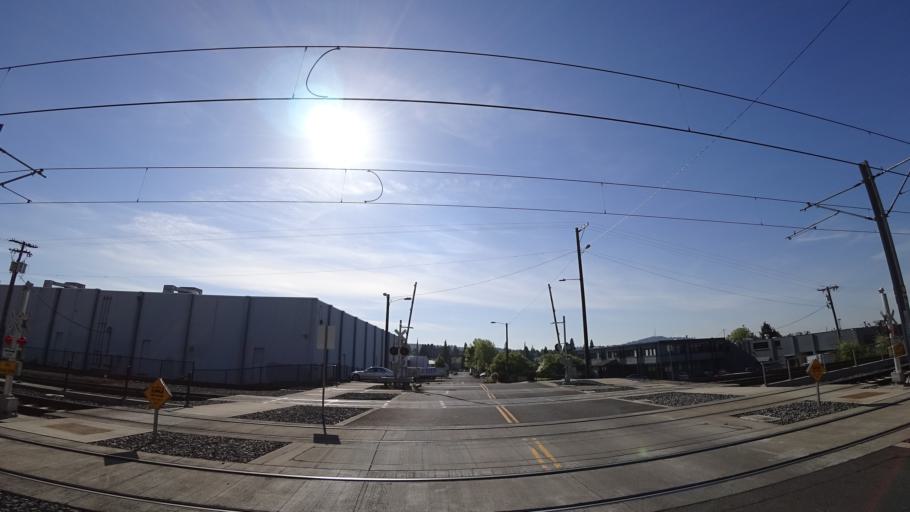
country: US
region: Oregon
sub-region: Clackamas County
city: Milwaukie
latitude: 45.4543
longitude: -122.6356
